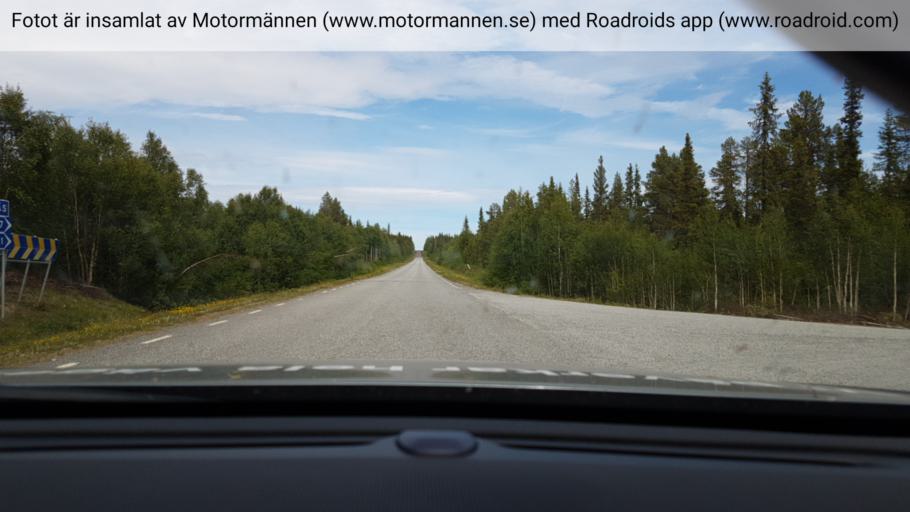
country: SE
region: Vaesterbotten
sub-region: Vilhelmina Kommun
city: Sjoberg
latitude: 65.1522
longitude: 16.3025
